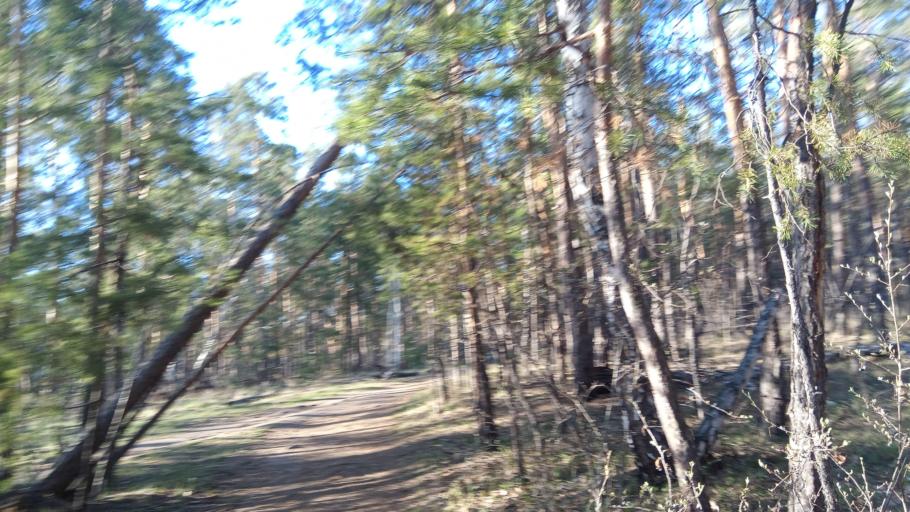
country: RU
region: Chelyabinsk
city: Novosineglazovskiy
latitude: 55.1251
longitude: 61.3376
